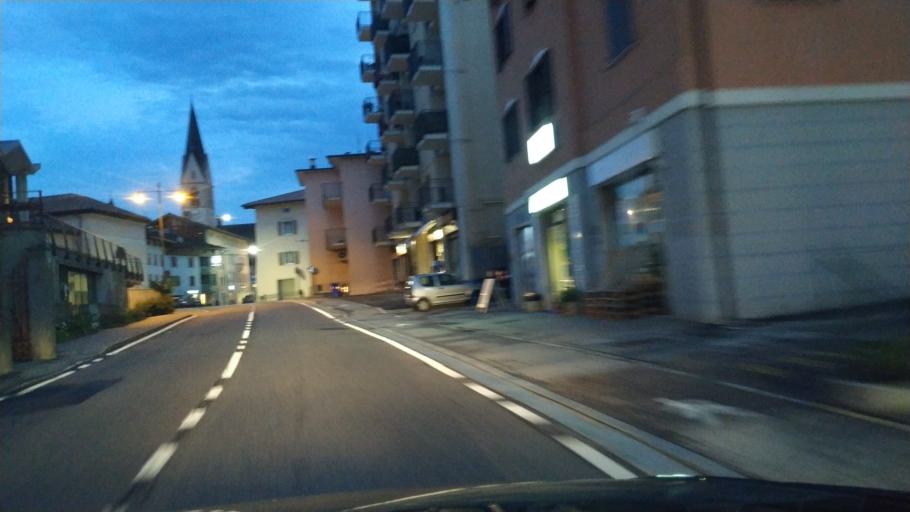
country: IT
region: Trentino-Alto Adige
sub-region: Provincia di Trento
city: Cles
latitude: 46.3664
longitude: 11.0357
